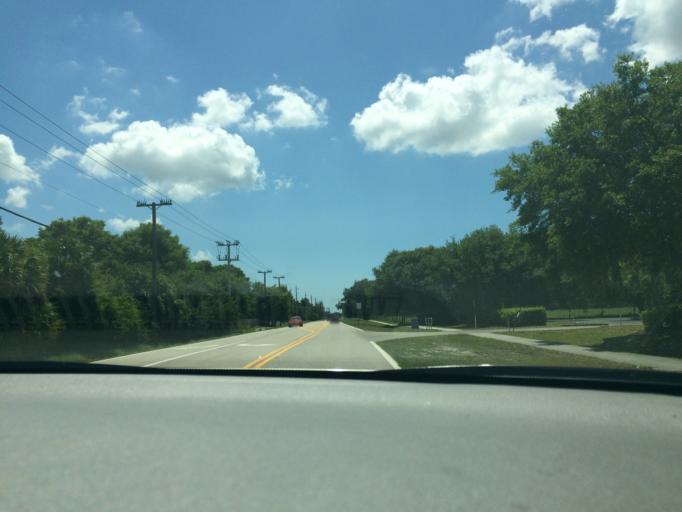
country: US
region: Florida
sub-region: Manatee County
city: Samoset
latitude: 27.4611
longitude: -82.4854
